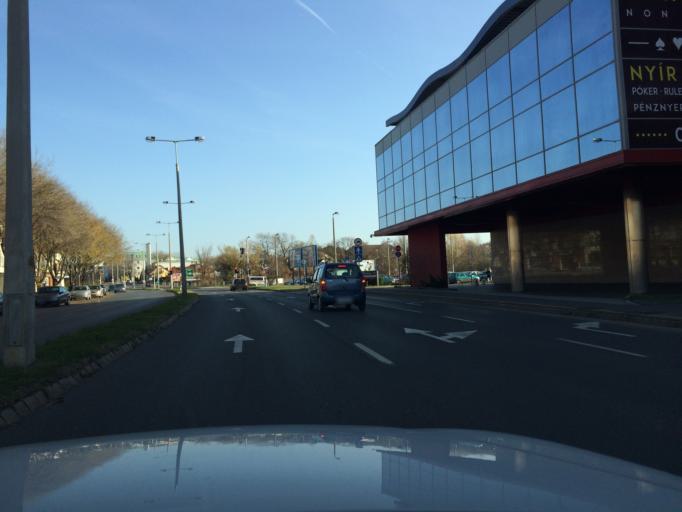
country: HU
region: Szabolcs-Szatmar-Bereg
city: Nyiregyhaza
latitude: 47.9556
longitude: 21.7321
